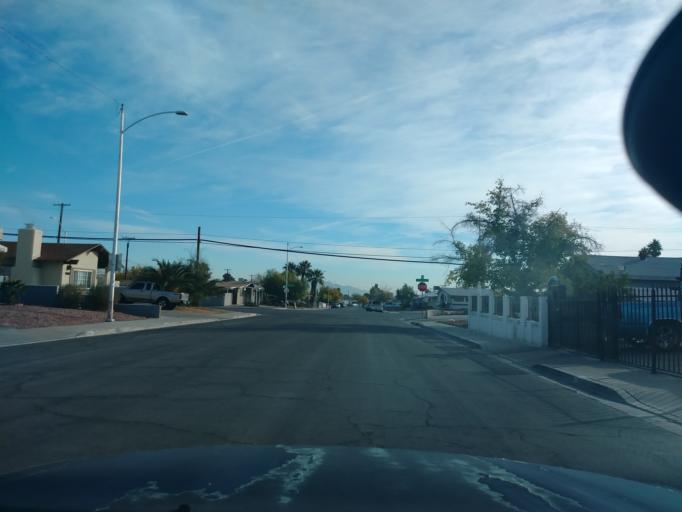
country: US
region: Nevada
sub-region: Clark County
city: Spring Valley
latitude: 36.1629
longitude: -115.2339
